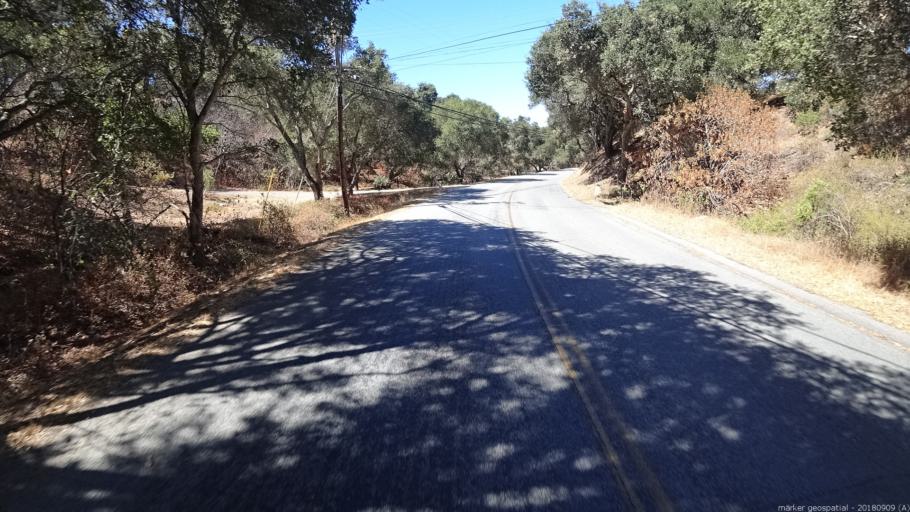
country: US
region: California
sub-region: Monterey County
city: Carmel Valley Village
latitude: 36.5501
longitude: -121.6834
